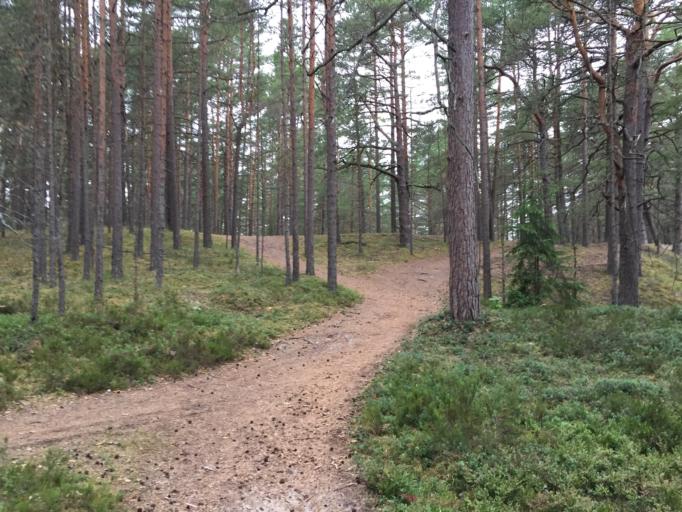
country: LV
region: Carnikava
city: Carnikava
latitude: 57.1212
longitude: 24.2192
